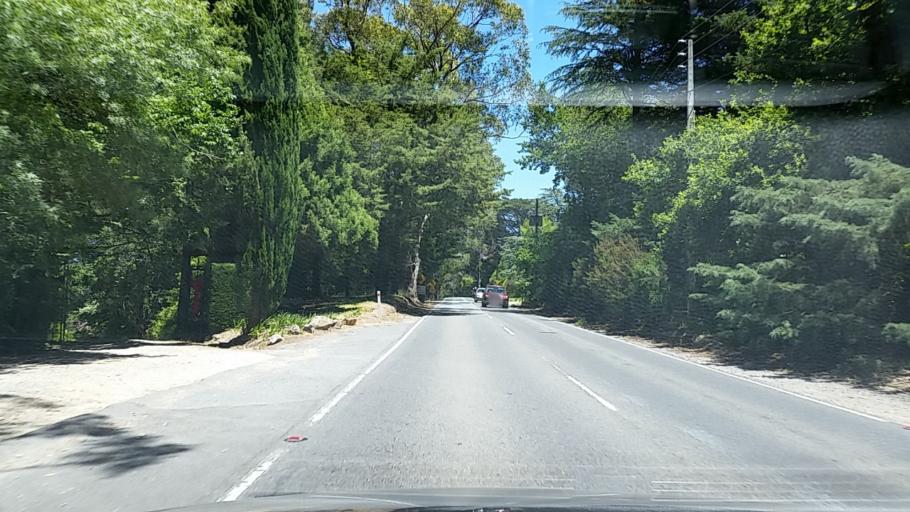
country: AU
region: South Australia
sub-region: Adelaide Hills
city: Crafers
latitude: -35.0046
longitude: 138.7000
